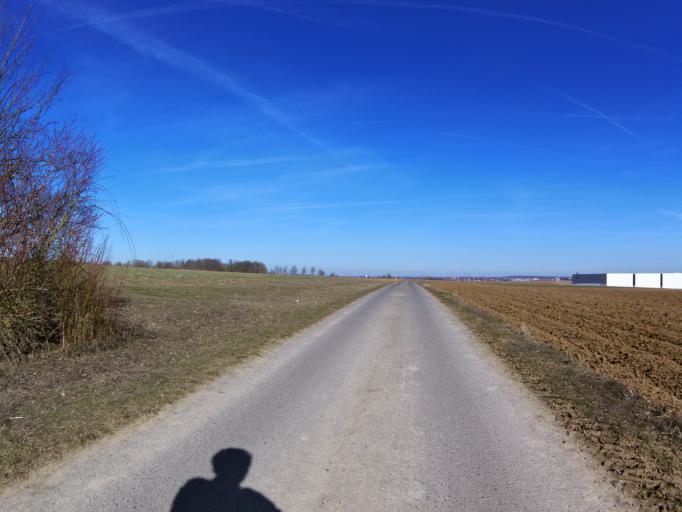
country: DE
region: Bavaria
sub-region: Regierungsbezirk Unterfranken
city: Kurnach
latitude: 49.8507
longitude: 10.0193
